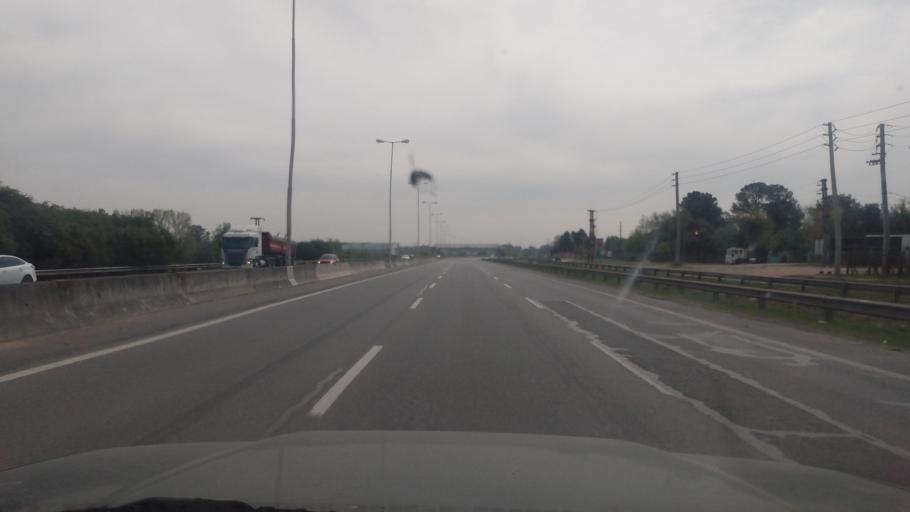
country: AR
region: Buenos Aires
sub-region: Partido de Pilar
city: Pilar
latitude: -34.4219
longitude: -59.0005
